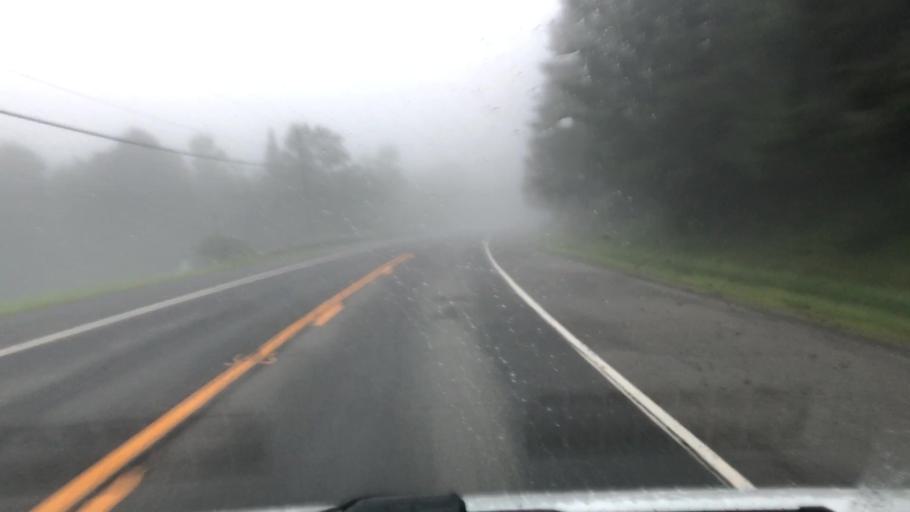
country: US
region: Massachusetts
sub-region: Berkshire County
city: Hinsdale
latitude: 42.5006
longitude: -73.0346
